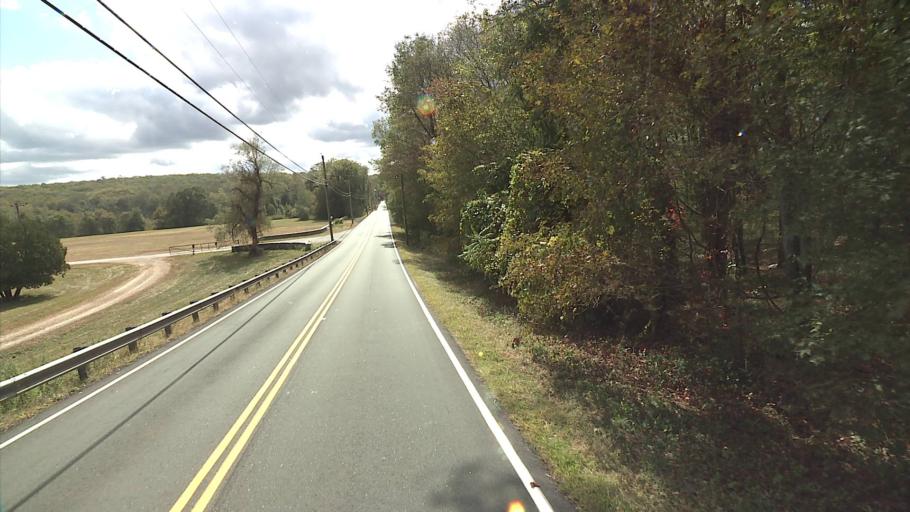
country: US
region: Connecticut
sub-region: Middlesex County
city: Higganum
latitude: 41.4032
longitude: -72.6047
